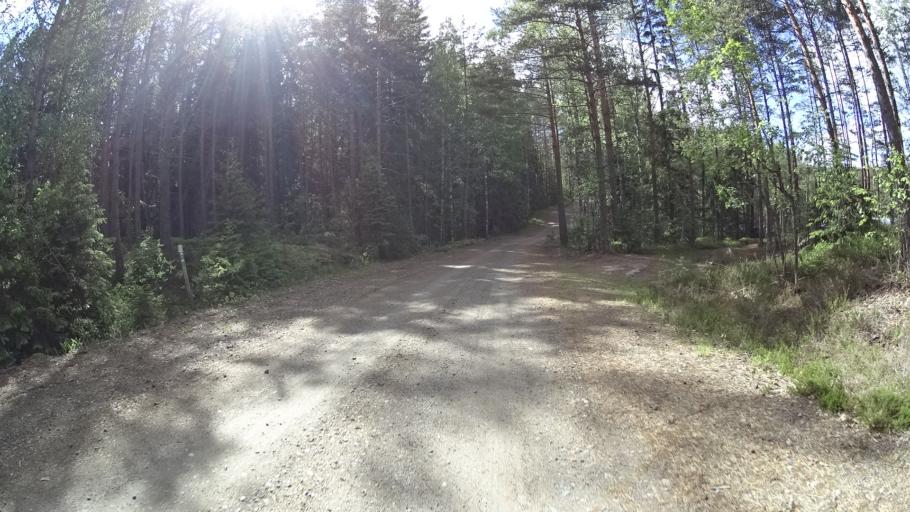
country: FI
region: Varsinais-Suomi
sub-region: Salo
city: Kisko
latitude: 60.1797
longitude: 23.5431
